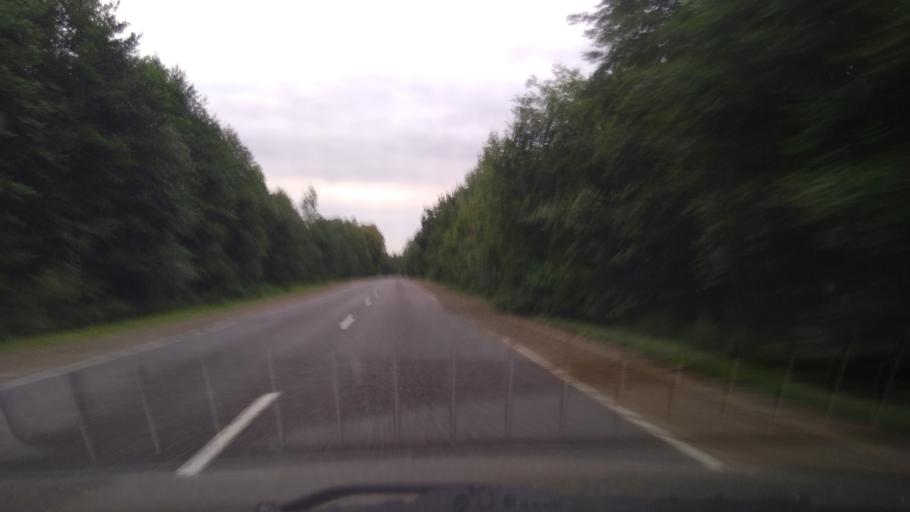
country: BY
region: Brest
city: Byaroza
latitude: 52.4102
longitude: 24.9940
